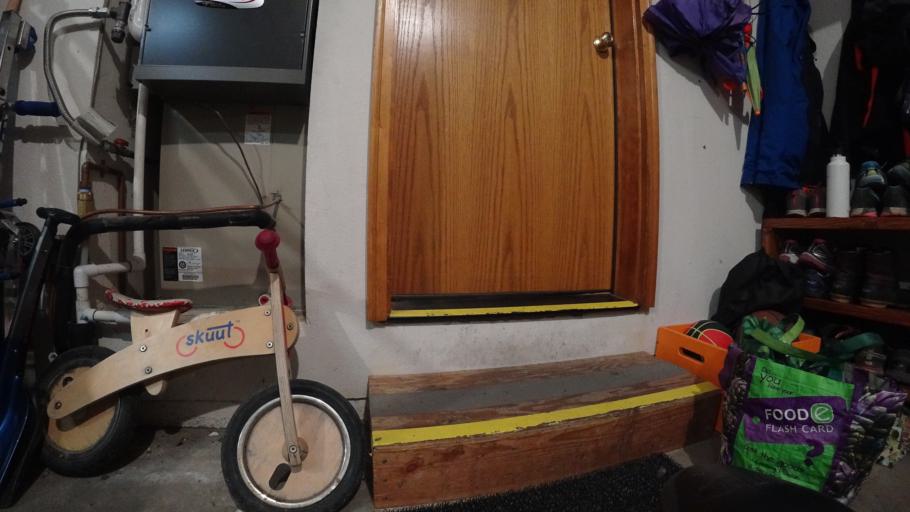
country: US
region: Oregon
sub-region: Deschutes County
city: Bend
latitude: 44.0376
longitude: -121.2742
